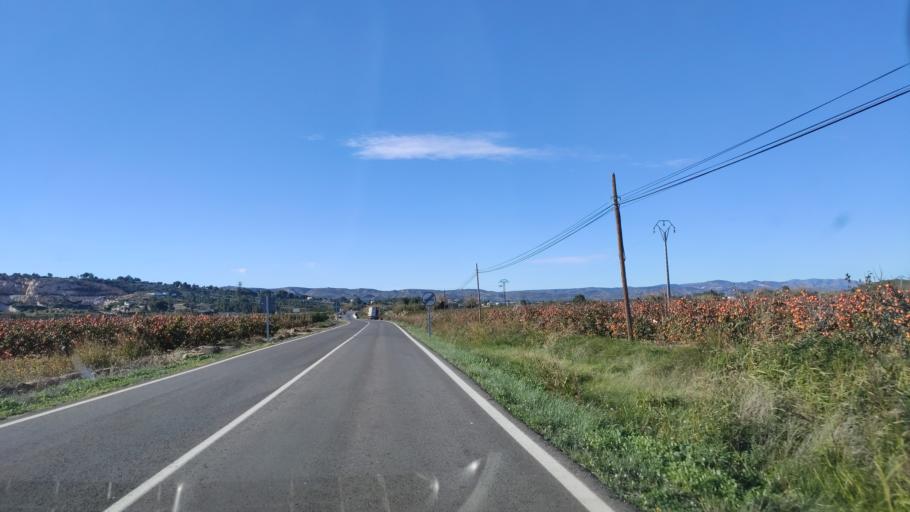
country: ES
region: Valencia
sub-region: Provincia de Valencia
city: Alberic
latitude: 39.1210
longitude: -0.5408
